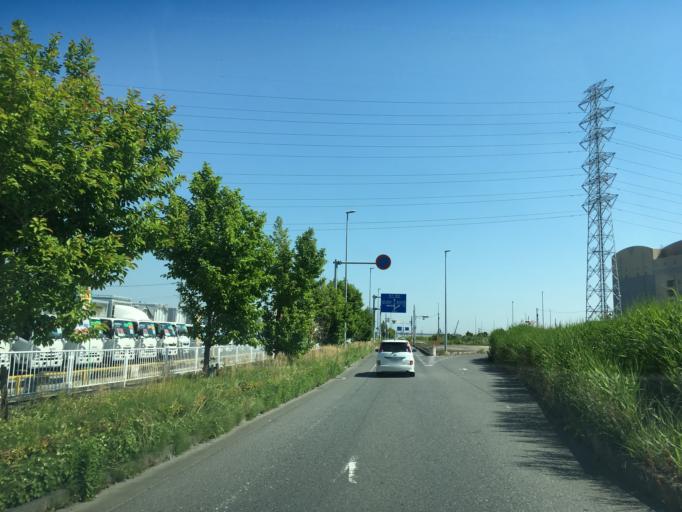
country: JP
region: Saitama
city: Yoshikawa
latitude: 35.8562
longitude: 139.8293
